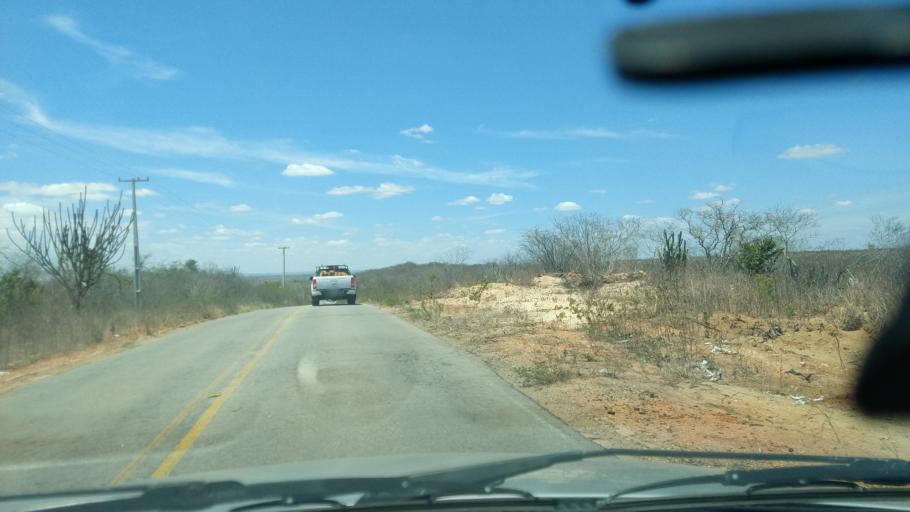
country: BR
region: Rio Grande do Norte
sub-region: Sao Paulo Do Potengi
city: Sao Paulo do Potengi
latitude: -5.9080
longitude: -35.6021
